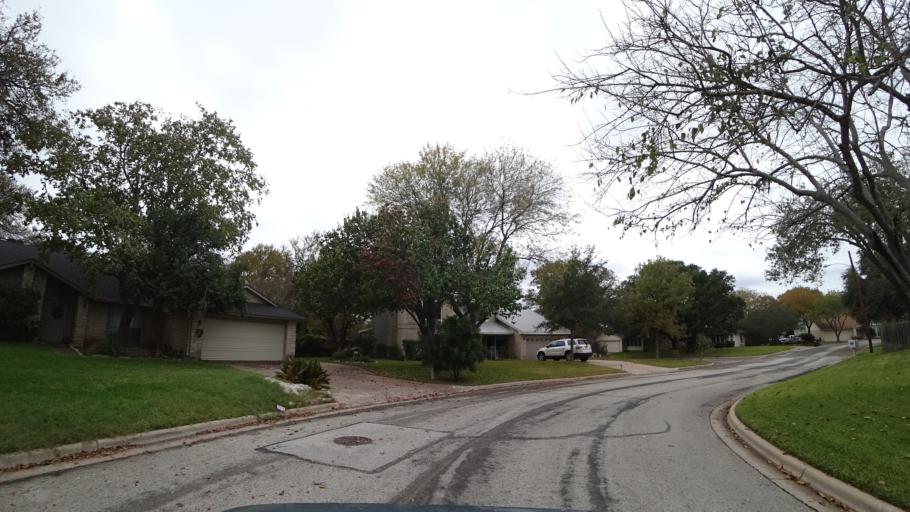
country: US
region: Texas
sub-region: Williamson County
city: Round Rock
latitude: 30.4869
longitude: -97.7057
